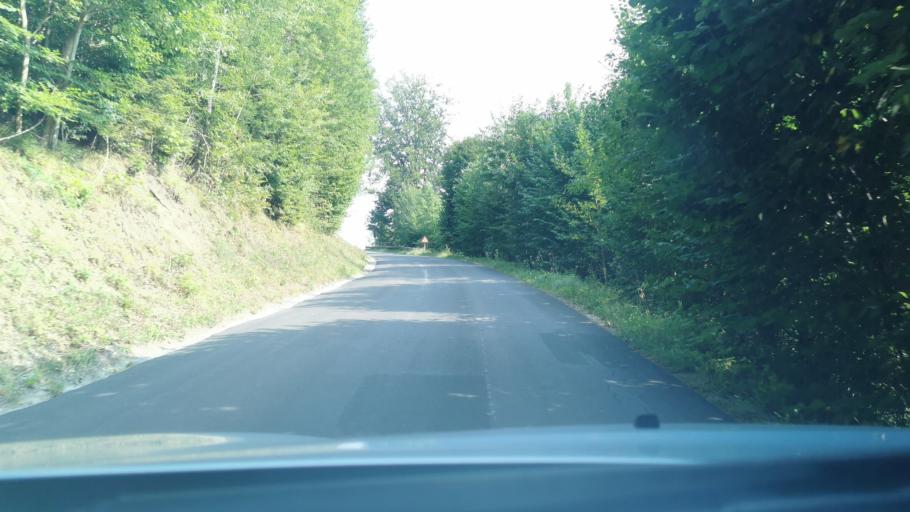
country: AT
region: Styria
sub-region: Politischer Bezirk Weiz
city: Strallegg
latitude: 47.3995
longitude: 15.6888
